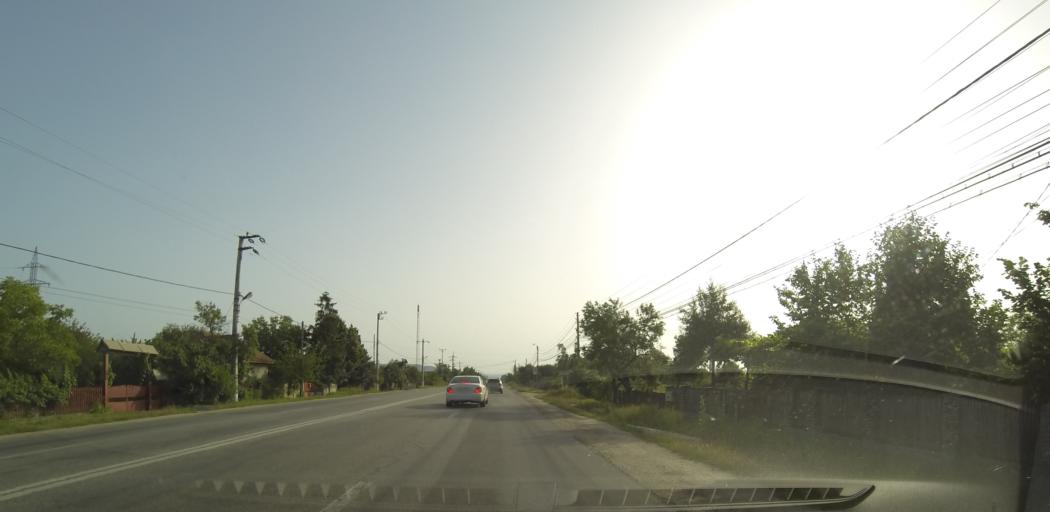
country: RO
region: Valcea
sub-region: Municipiul Ramnicu Valcea
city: Stolniceni
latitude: 45.0387
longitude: 24.3044
